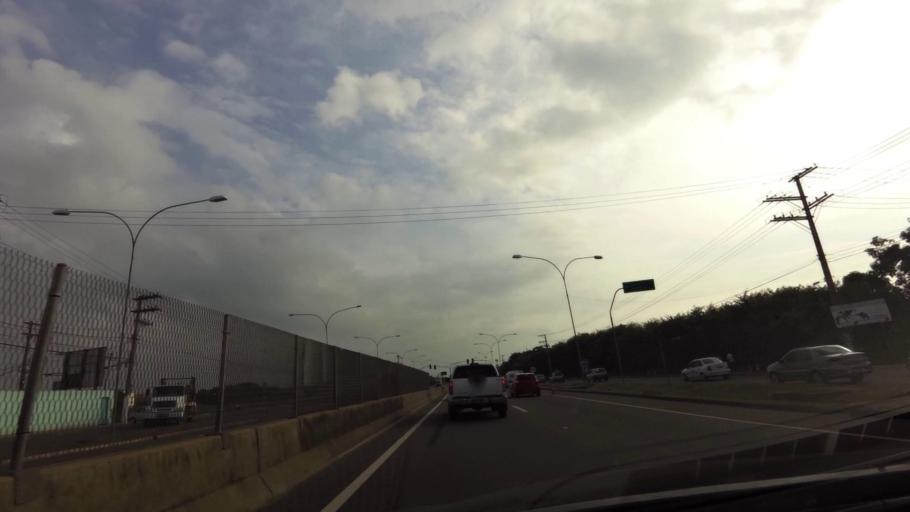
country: BR
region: Espirito Santo
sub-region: Vila Velha
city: Vila Velha
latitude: -20.4201
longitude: -40.3289
